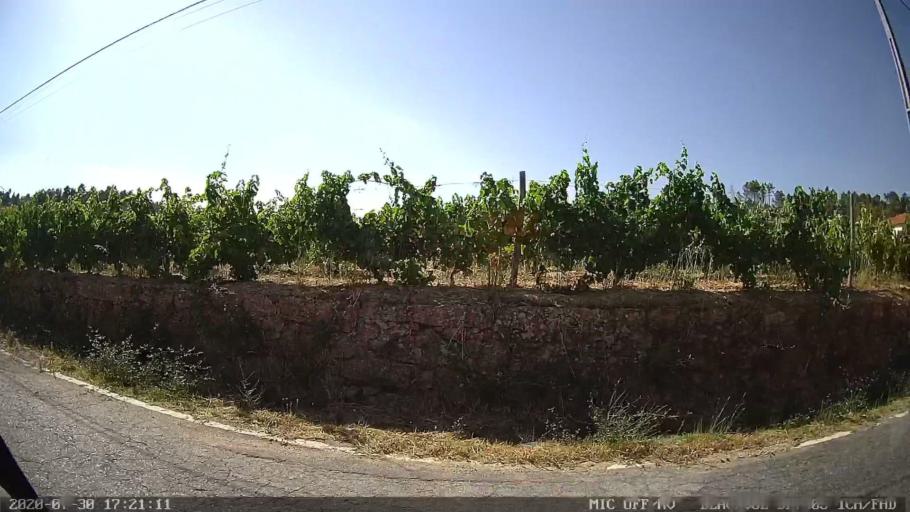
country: PT
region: Vila Real
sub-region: Sabrosa
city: Sabrosa
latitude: 41.2954
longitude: -7.4795
